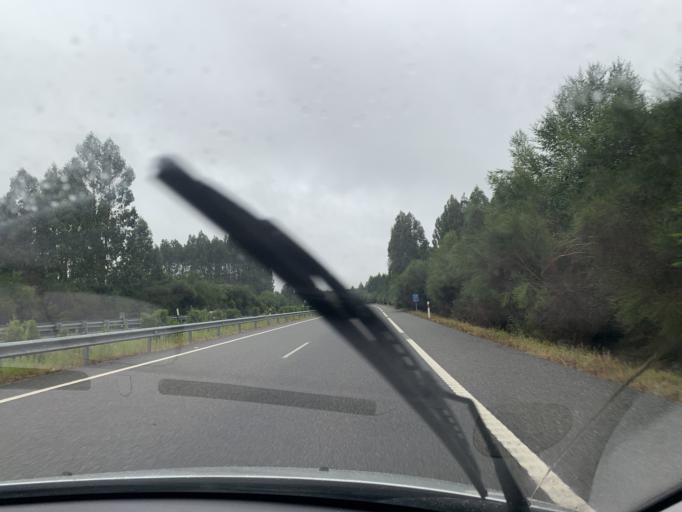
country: ES
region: Galicia
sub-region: Provincia de Lugo
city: Vilalba
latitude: 43.3222
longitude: -7.6582
